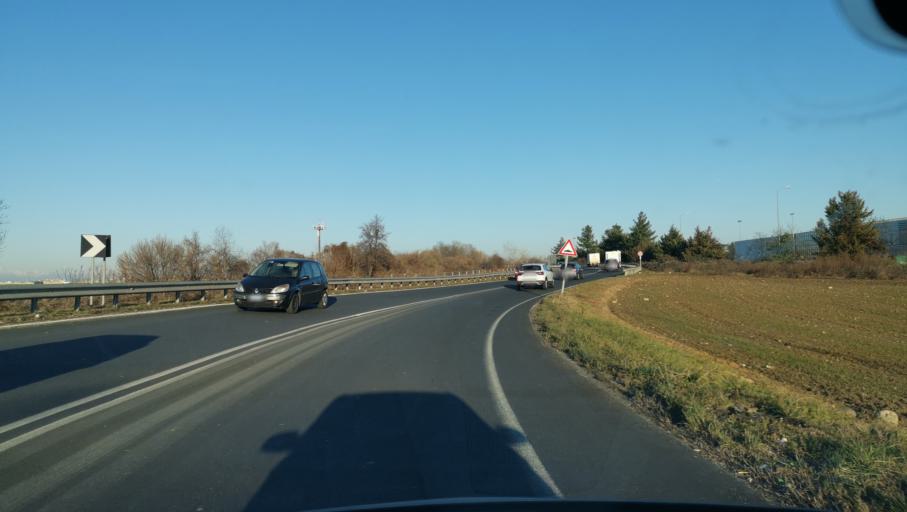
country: IT
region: Piedmont
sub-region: Provincia di Torino
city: Tetti Neirotti
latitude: 45.0378
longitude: 7.5547
